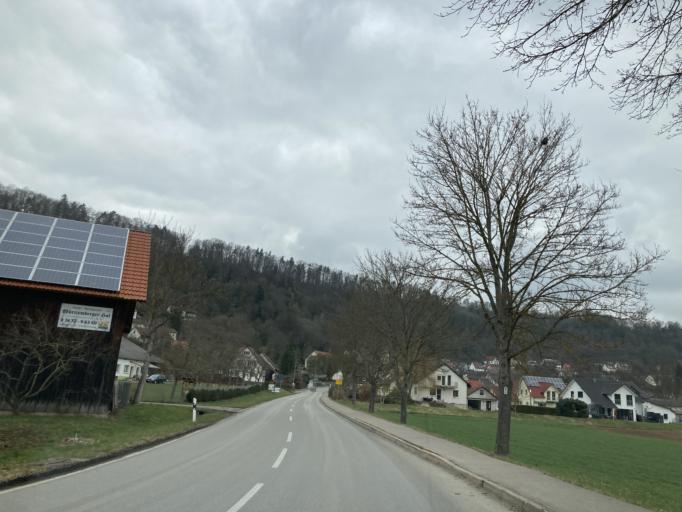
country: DE
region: Baden-Wuerttemberg
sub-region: Tuebingen Region
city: Haigerloch
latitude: 48.4453
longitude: 8.8004
